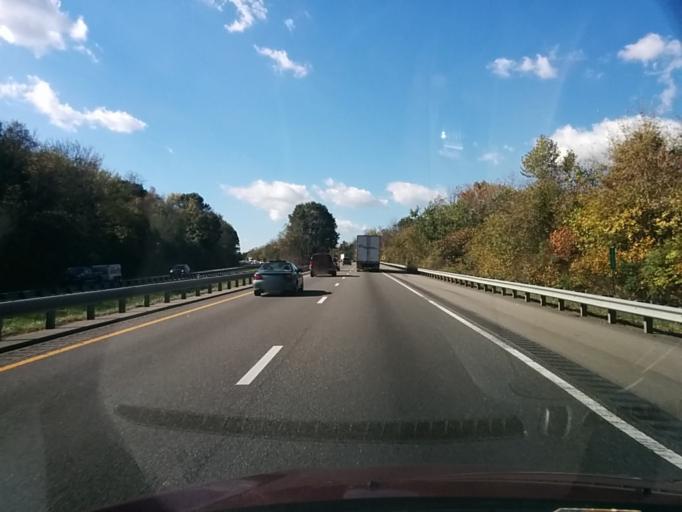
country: US
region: Virginia
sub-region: Botetourt County
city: Buchanan
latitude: 37.5132
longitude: -79.7367
